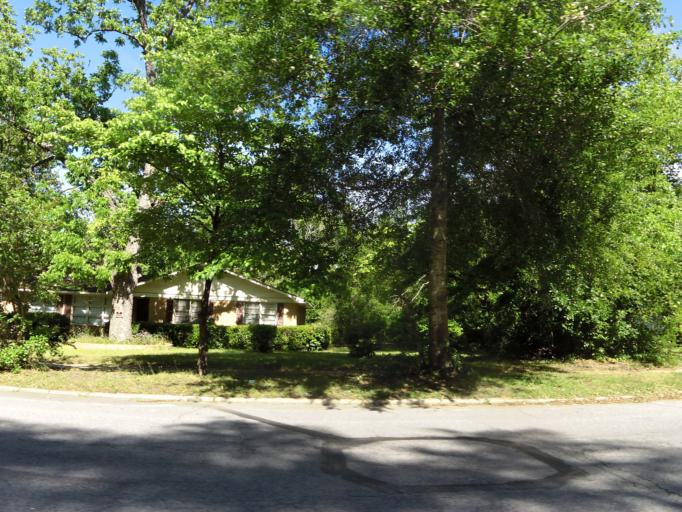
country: US
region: South Carolina
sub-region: Bamberg County
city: Denmark
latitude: 33.3168
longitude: -81.1434
